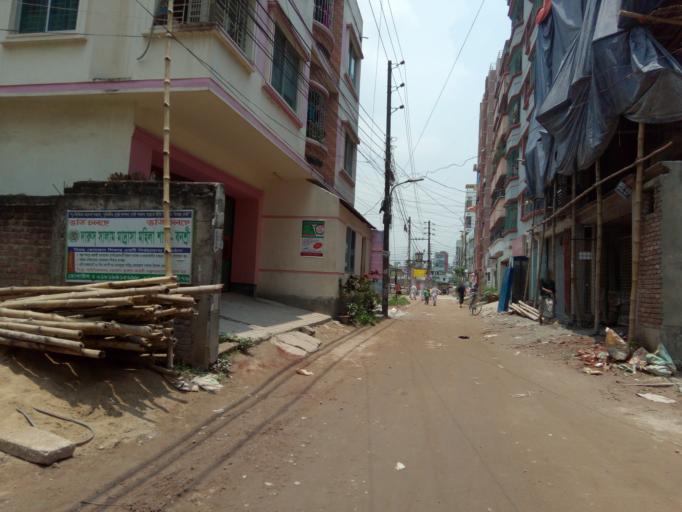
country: BD
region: Dhaka
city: Paltan
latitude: 23.7594
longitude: 90.4425
